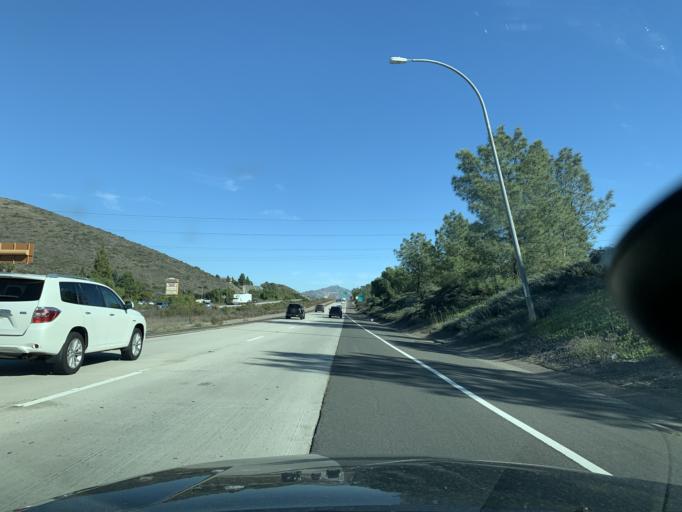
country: US
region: California
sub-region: San Diego County
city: Poway
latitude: 32.9587
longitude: -117.1125
